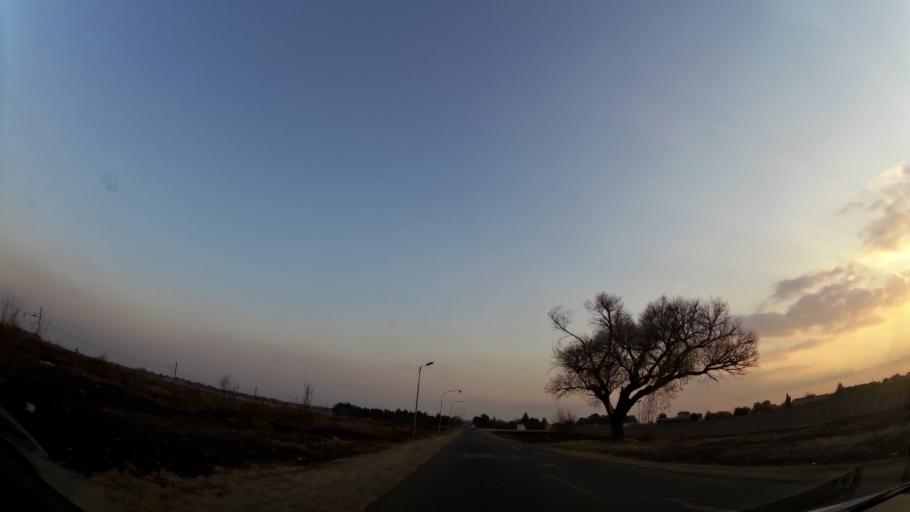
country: ZA
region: Gauteng
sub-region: Ekurhuleni Metropolitan Municipality
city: Springs
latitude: -26.3309
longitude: 28.4416
